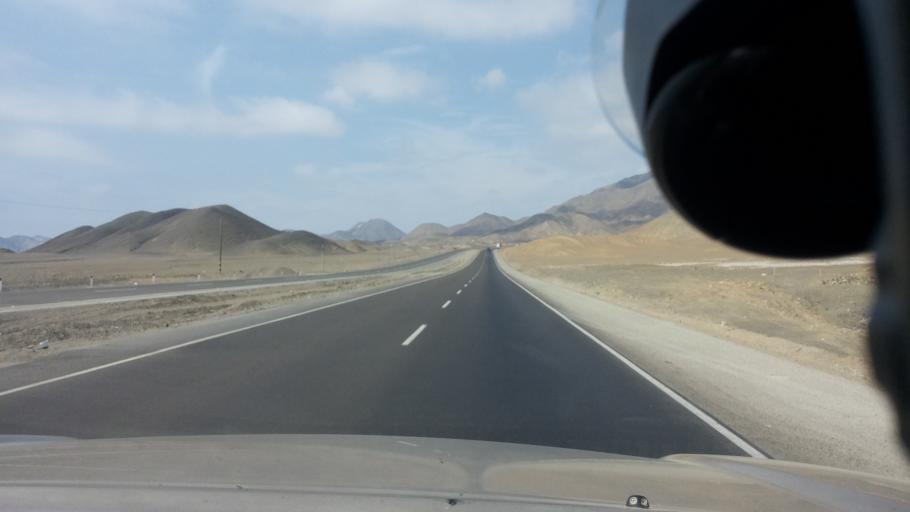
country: PE
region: Ancash
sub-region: Provincia de Huarmey
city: La Caleta Culebras
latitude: -9.9142
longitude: -78.2184
